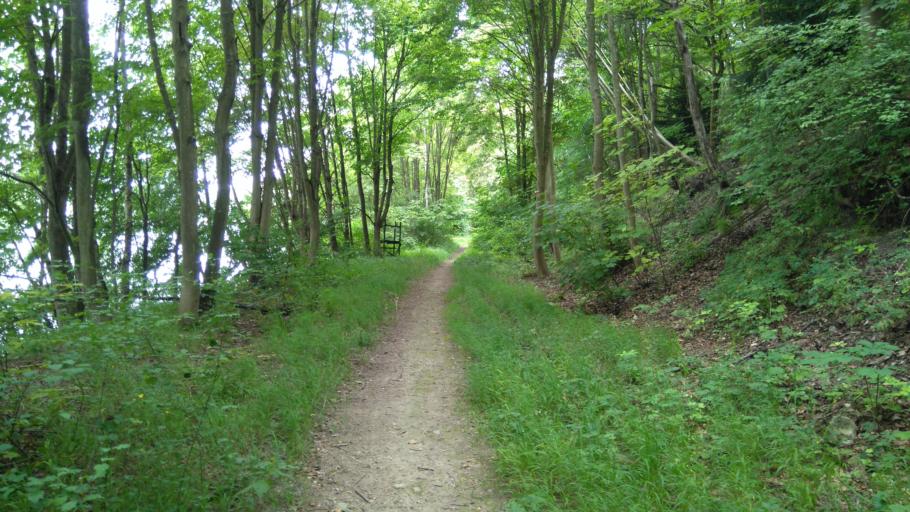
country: FR
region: Picardie
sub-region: Departement de l'Oise
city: Saint-Maximin
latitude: 49.2408
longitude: 2.4517
